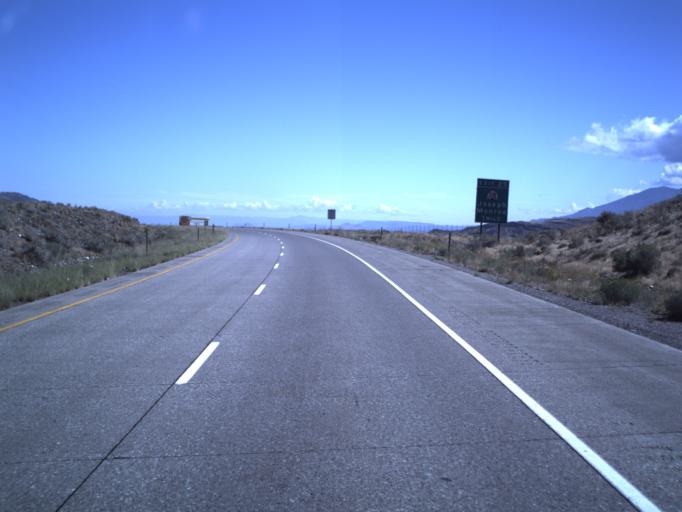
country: US
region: Utah
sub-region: Sevier County
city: Monroe
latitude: 38.6048
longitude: -112.2359
